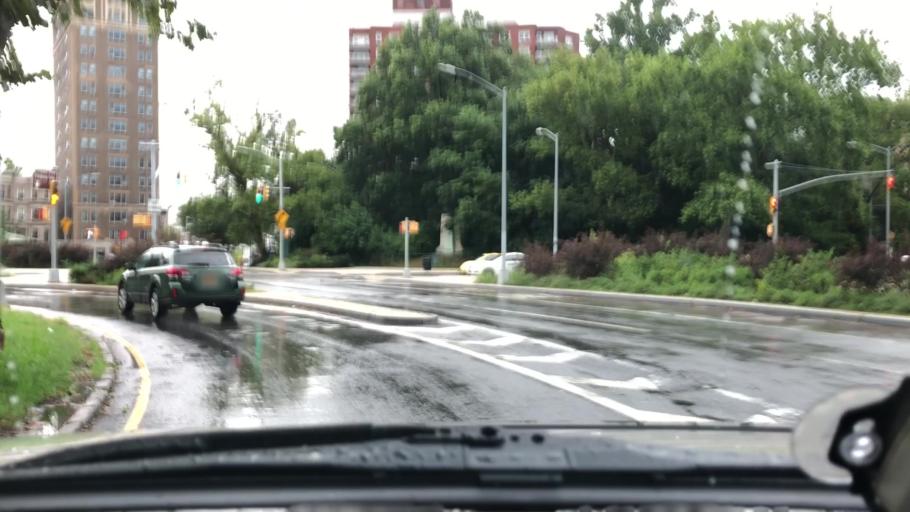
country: US
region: New York
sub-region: Kings County
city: Brooklyn
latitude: 40.6743
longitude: -73.9698
